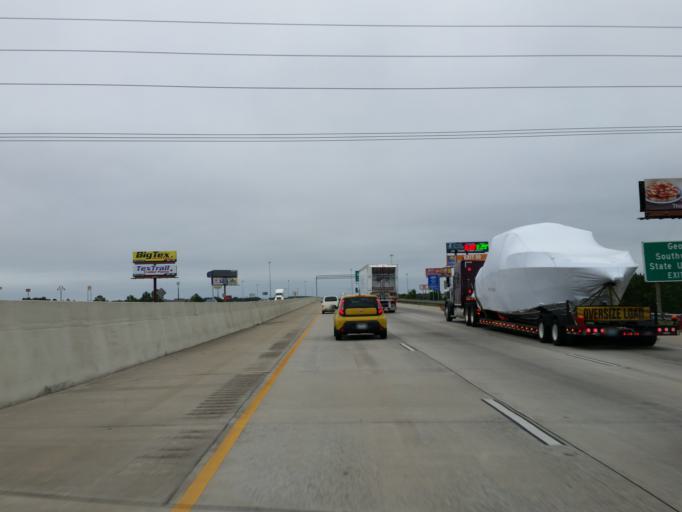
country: US
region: Georgia
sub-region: Crisp County
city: Cordele
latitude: 31.9662
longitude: -83.7526
